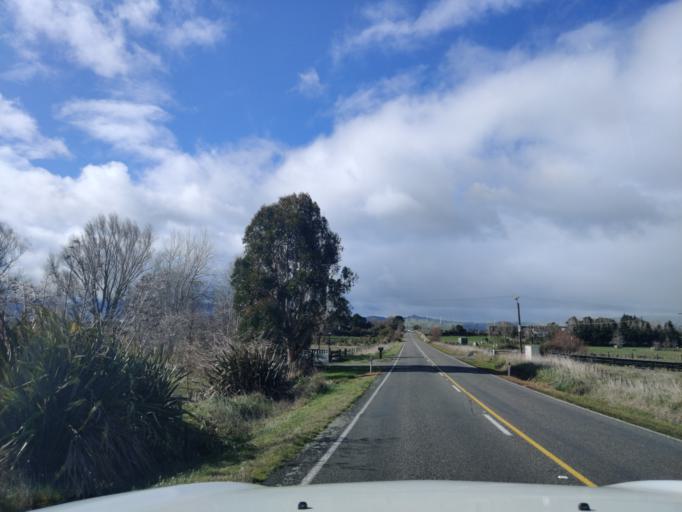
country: NZ
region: Manawatu-Wanganui
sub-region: Palmerston North City
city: Palmerston North
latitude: -40.2895
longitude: 175.7093
